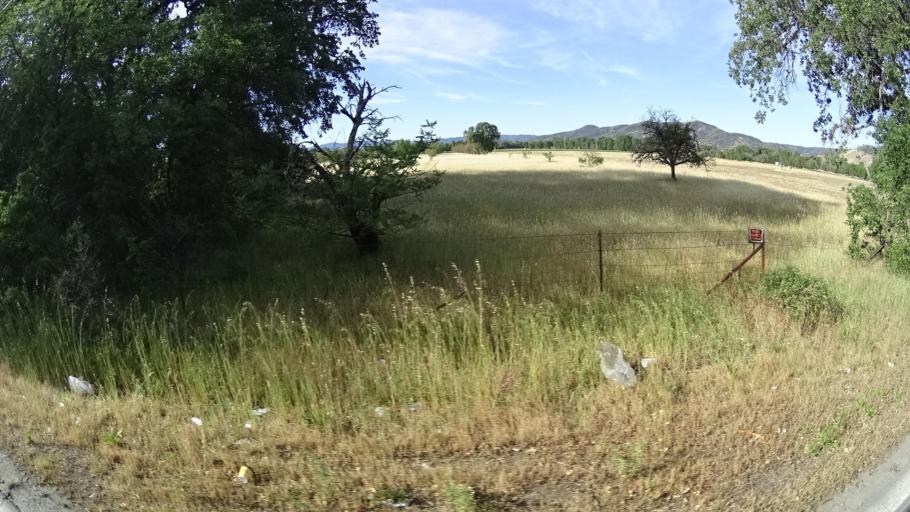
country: US
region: California
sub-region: Lake County
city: Lakeport
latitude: 39.0112
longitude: -122.9011
